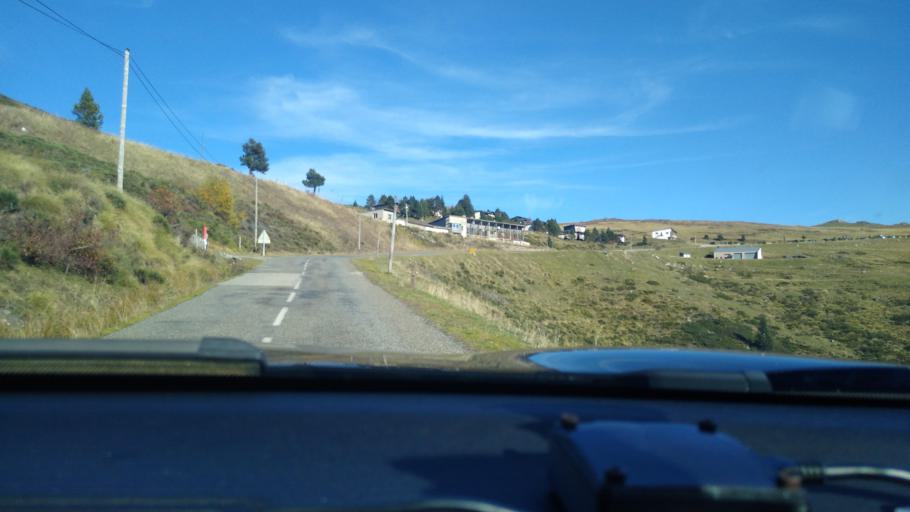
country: FR
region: Midi-Pyrenees
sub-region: Departement de l'Ariege
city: Ax-les-Thermes
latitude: 42.7336
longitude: 1.9814
